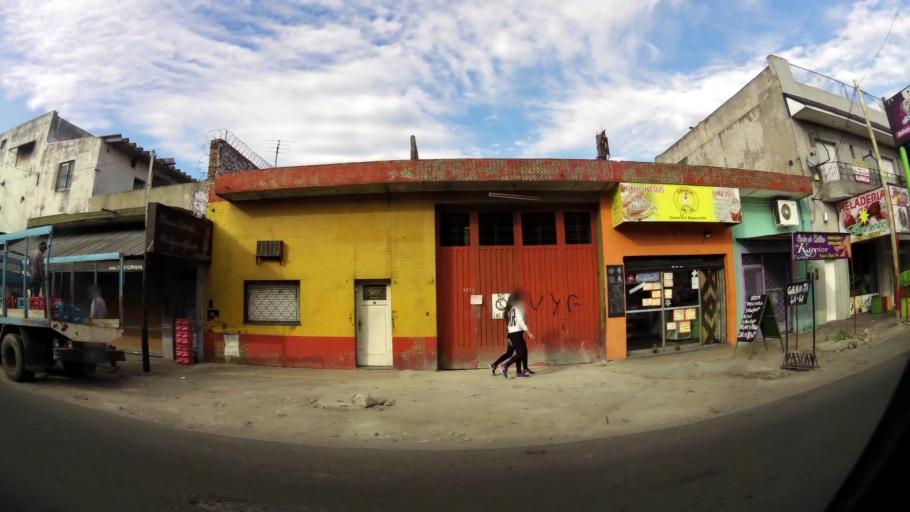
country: AR
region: Buenos Aires
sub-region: Partido de Lanus
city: Lanus
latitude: -34.7118
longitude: -58.3511
